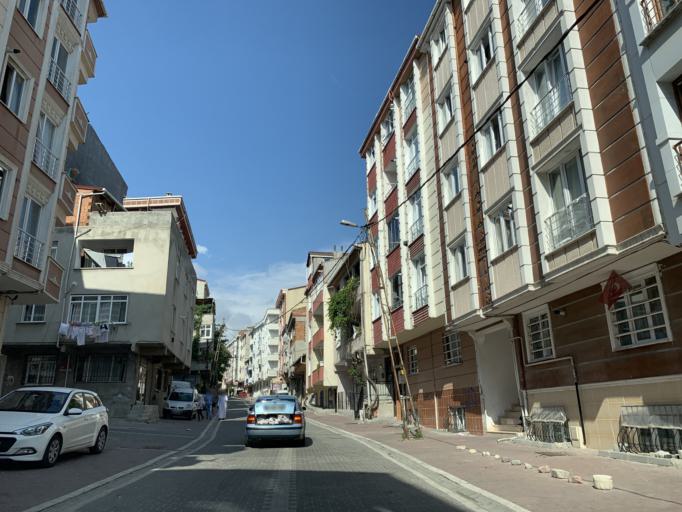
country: TR
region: Istanbul
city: Esenyurt
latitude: 41.0346
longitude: 28.6693
